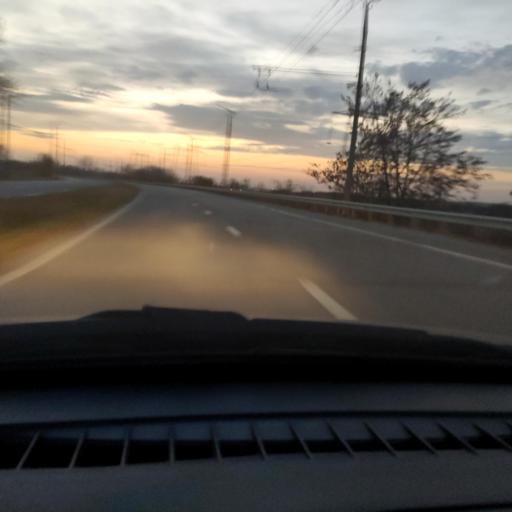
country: RU
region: Samara
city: Povolzhskiy
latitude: 53.5487
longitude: 49.5951
